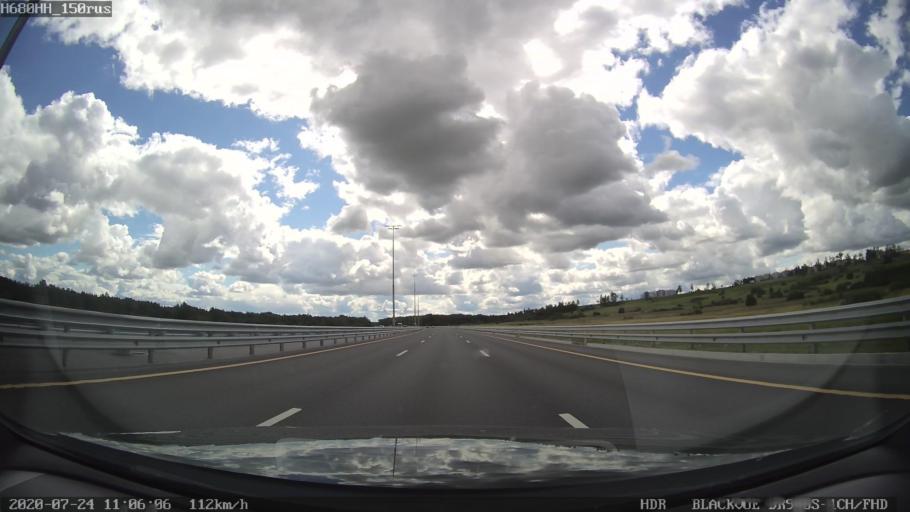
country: RU
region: St.-Petersburg
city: Shushary
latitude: 59.7680
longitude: 30.3671
